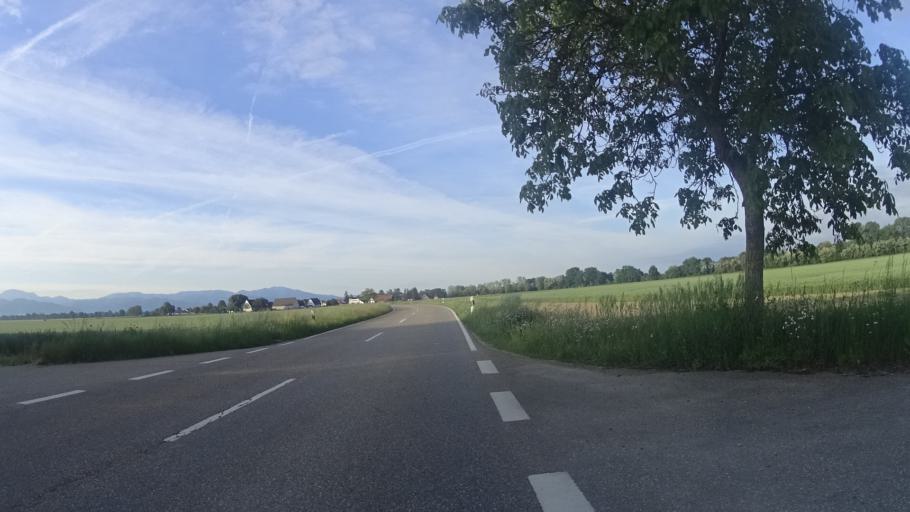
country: DE
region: Baden-Wuerttemberg
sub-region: Freiburg Region
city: Hartheim
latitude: 47.9737
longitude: 7.6440
